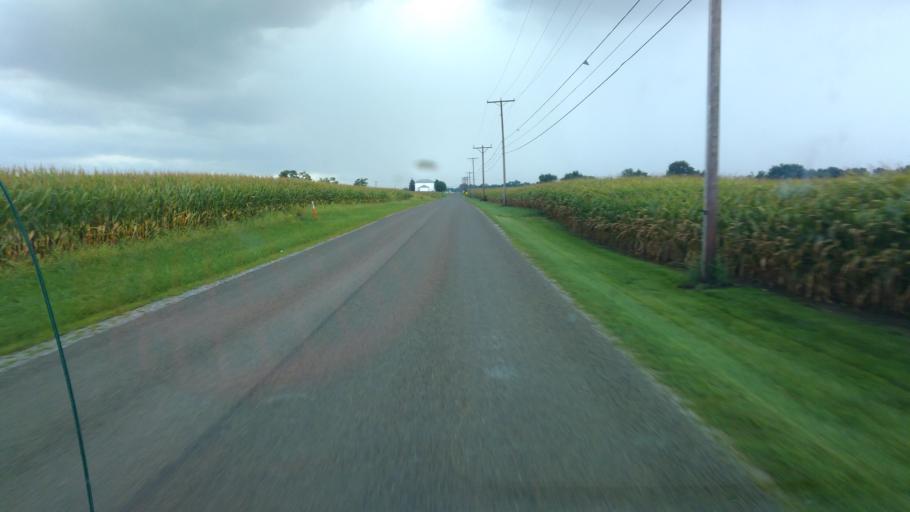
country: US
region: Ohio
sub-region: Hardin County
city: Kenton
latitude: 40.6620
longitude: -83.5761
